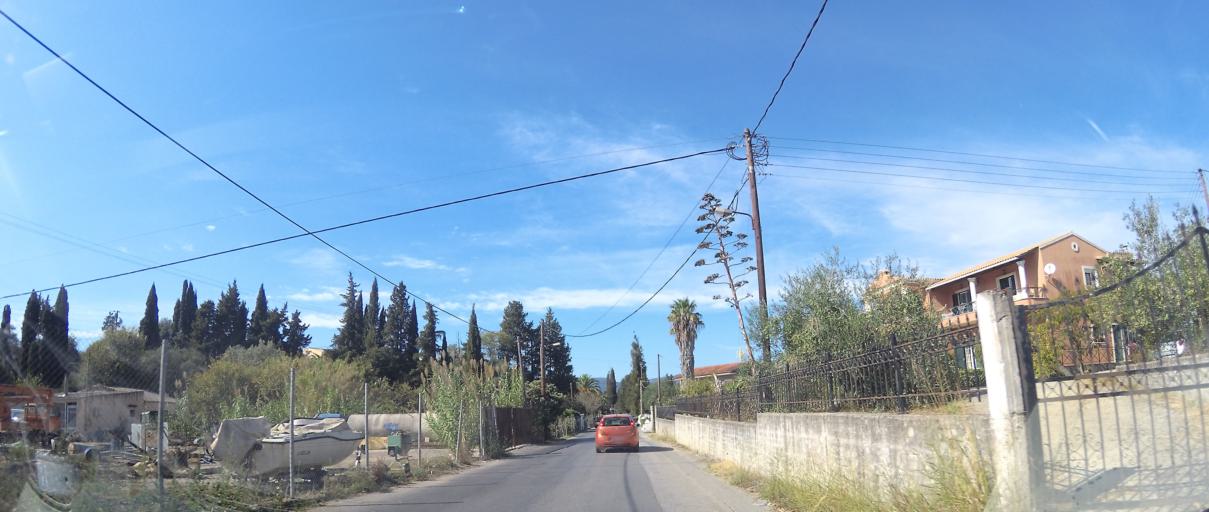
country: GR
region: Ionian Islands
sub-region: Nomos Kerkyras
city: Kontokali
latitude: 39.6474
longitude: 19.8446
